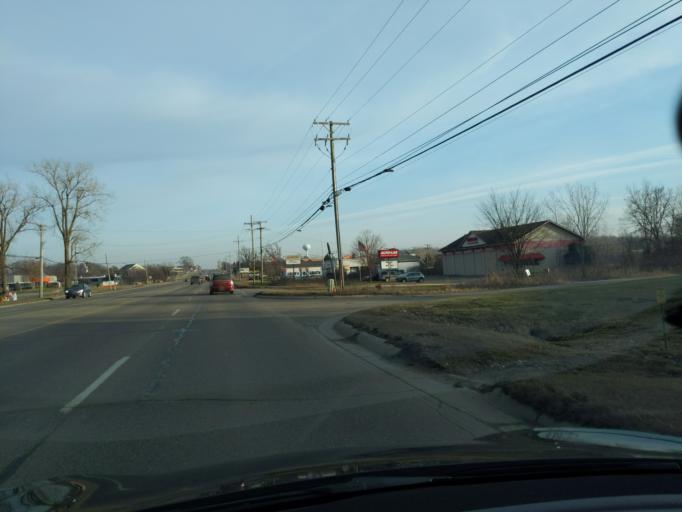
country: US
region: Michigan
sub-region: Livingston County
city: Howell
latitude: 42.5939
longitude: -83.8937
